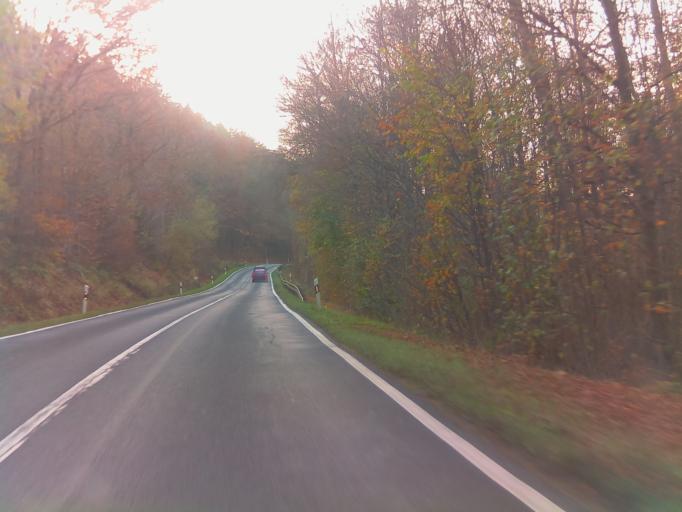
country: DE
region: Bavaria
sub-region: Regierungsbezirk Unterfranken
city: Bad Bruckenau
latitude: 50.3027
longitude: 9.7687
